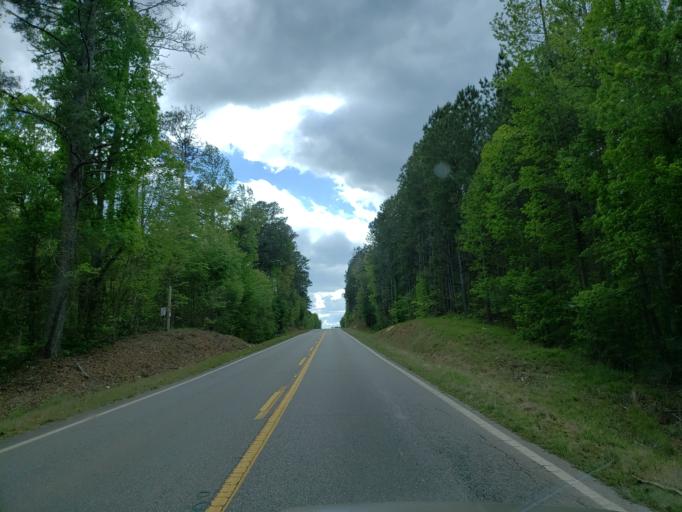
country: US
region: Georgia
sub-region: Haralson County
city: Tallapoosa
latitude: 33.7466
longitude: -85.3785
